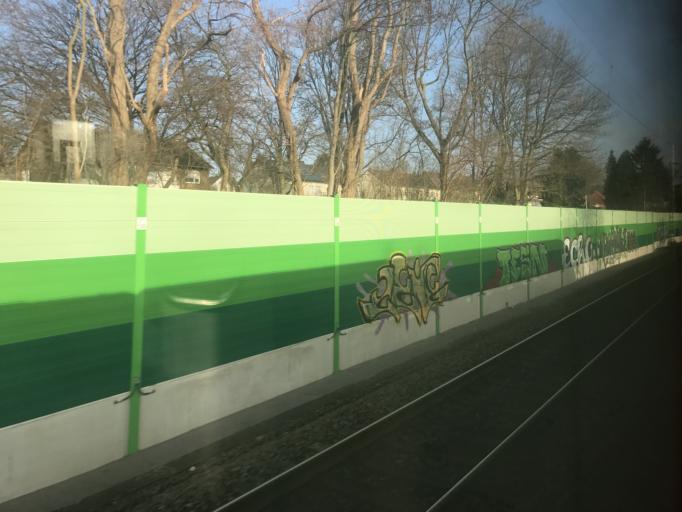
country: DE
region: North Rhine-Westphalia
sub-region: Regierungsbezirk Munster
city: Gelsenkirchen
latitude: 51.4611
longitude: 7.0827
